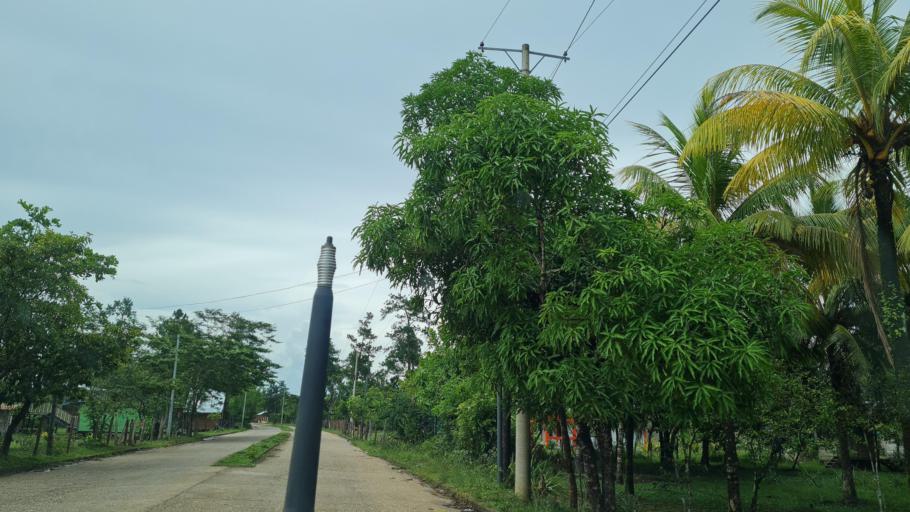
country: NI
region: Atlantico Norte (RAAN)
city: Waspam
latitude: 14.7269
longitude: -83.9713
